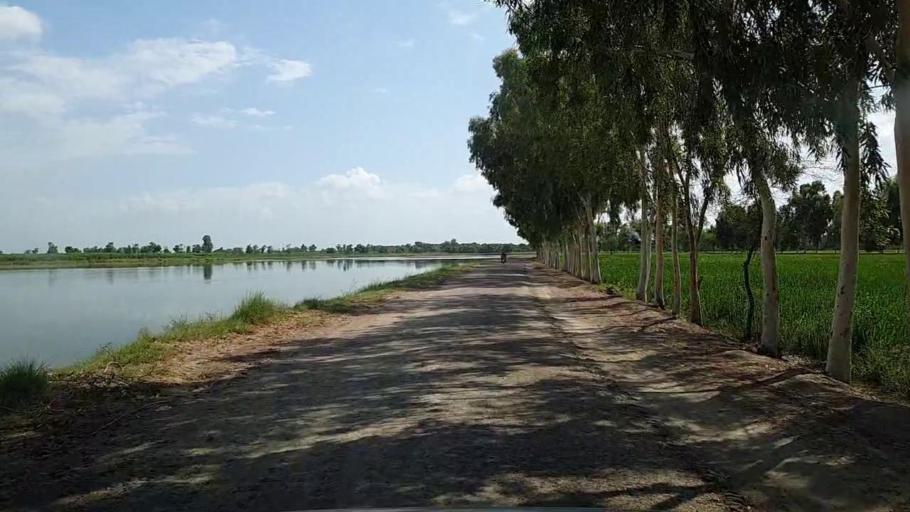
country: PK
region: Sindh
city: Bhiria
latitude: 26.9147
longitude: 68.2289
